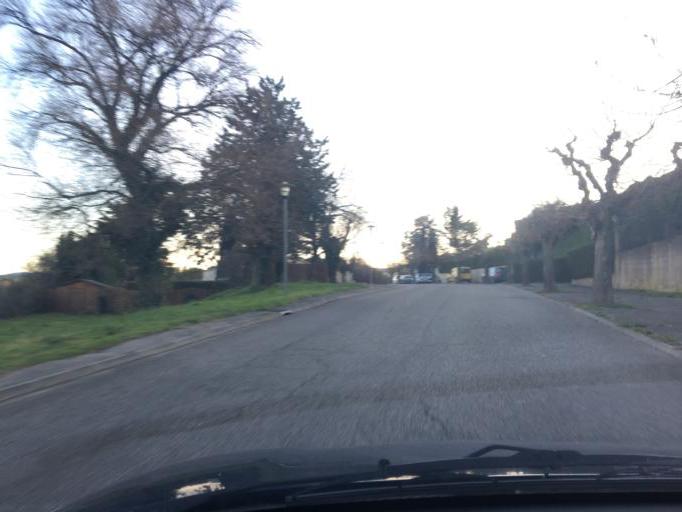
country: FR
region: Provence-Alpes-Cote d'Azur
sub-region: Departement des Bouches-du-Rhone
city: Mallemort
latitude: 43.7282
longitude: 5.1854
